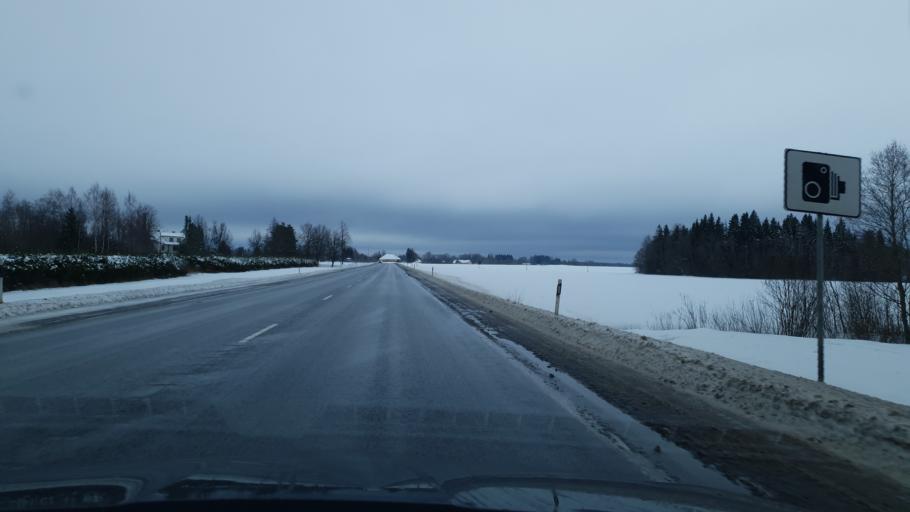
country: EE
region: Jogevamaa
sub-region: Poltsamaa linn
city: Poltsamaa
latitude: 58.6098
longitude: 26.1986
